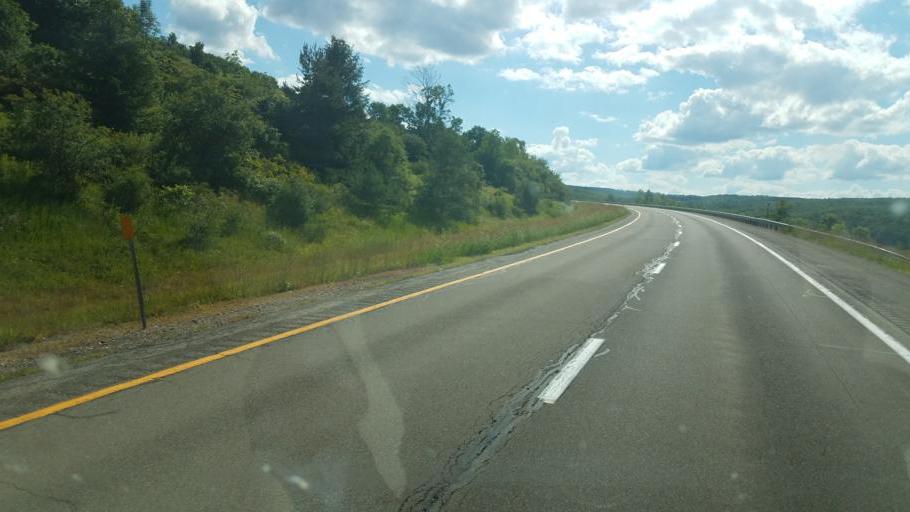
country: US
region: New York
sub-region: Allegany County
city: Alfred
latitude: 42.3203
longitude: -77.8319
